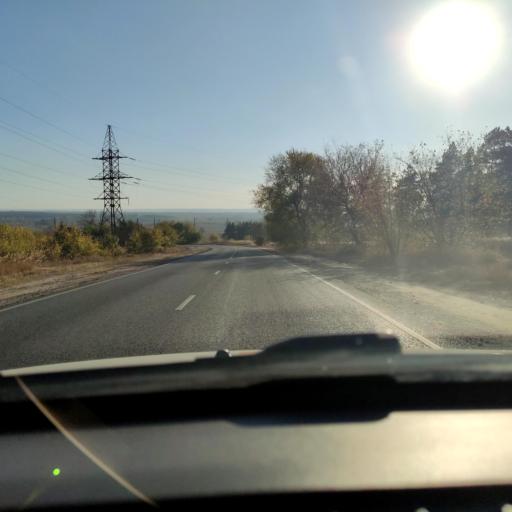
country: RU
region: Voronezj
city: Shilovo
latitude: 51.5558
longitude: 39.1337
